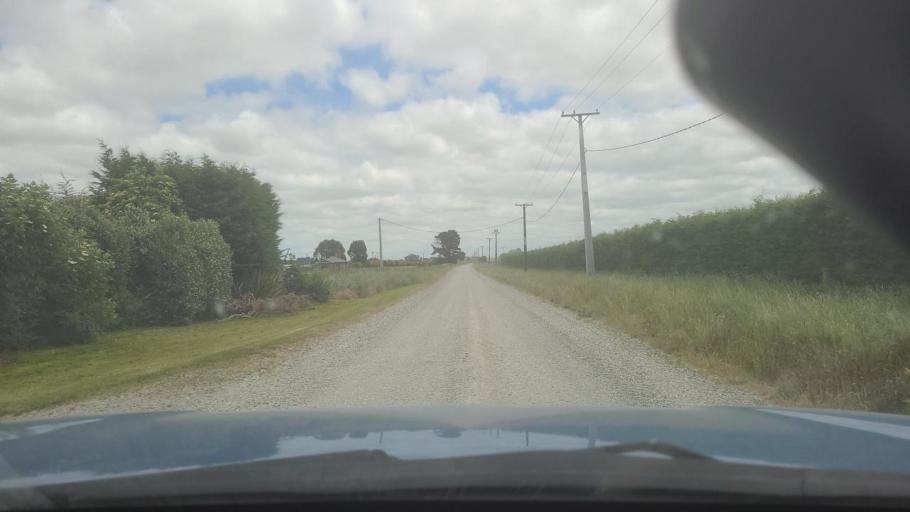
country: NZ
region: Southland
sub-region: Invercargill City
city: Invercargill
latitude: -46.2990
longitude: 168.3240
